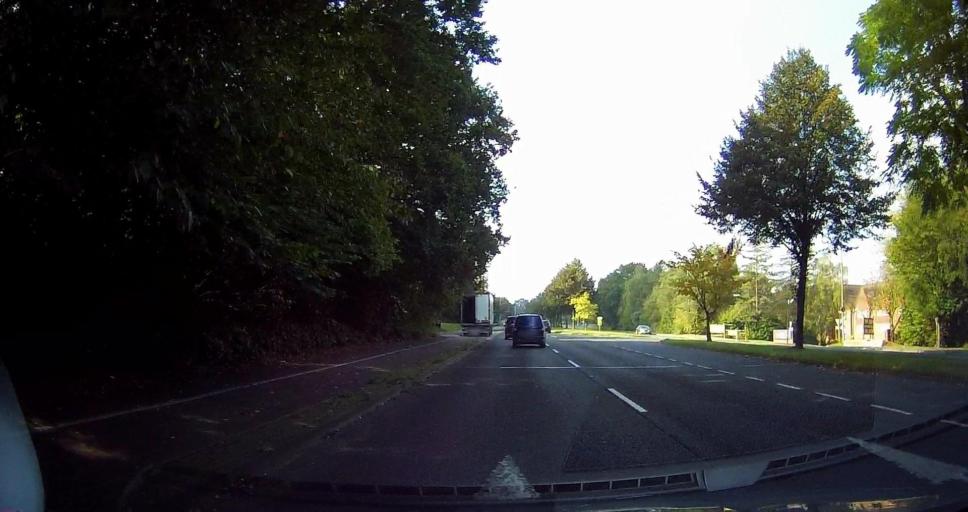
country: GB
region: England
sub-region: Kent
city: Ashford
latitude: 51.1572
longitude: 0.8664
